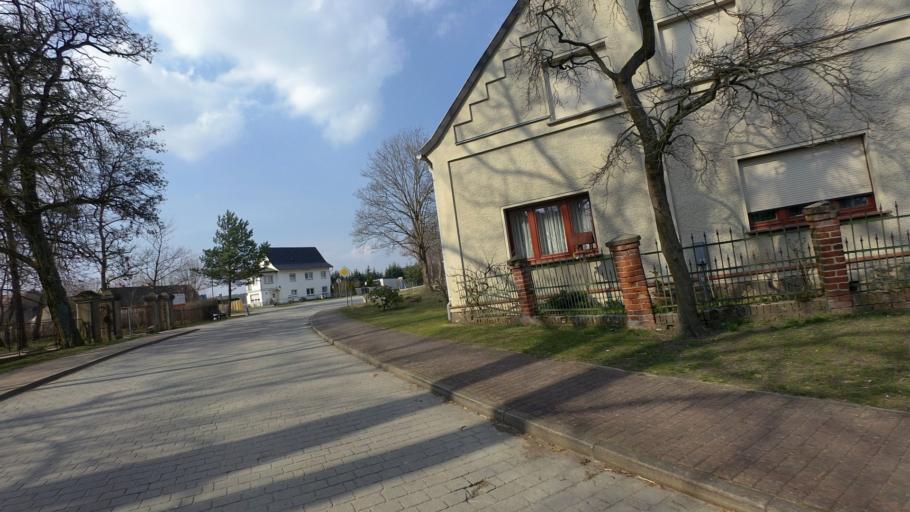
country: DE
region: Brandenburg
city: Dahme
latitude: 51.9417
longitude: 13.4432
